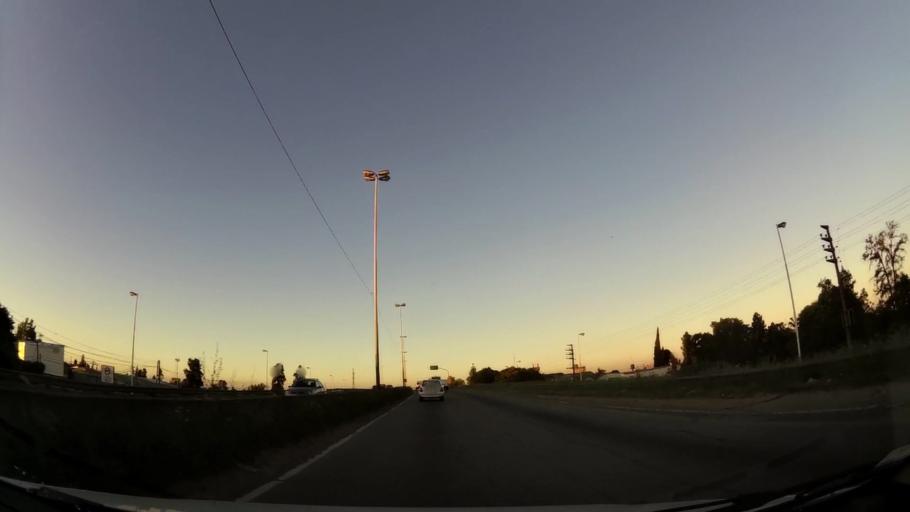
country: AR
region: Buenos Aires
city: Pontevedra
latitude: -34.7627
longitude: -58.6167
